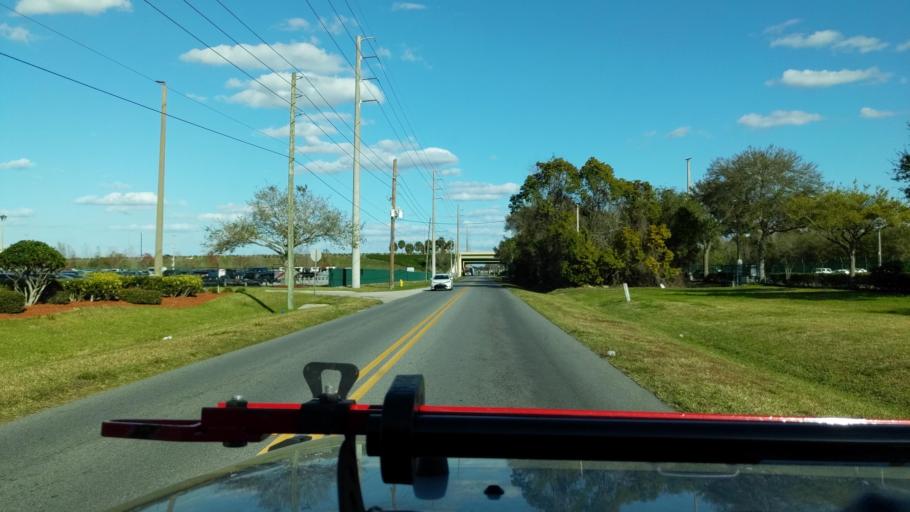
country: US
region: Florida
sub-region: Orange County
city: Ocoee
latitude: 28.5586
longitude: -81.5635
